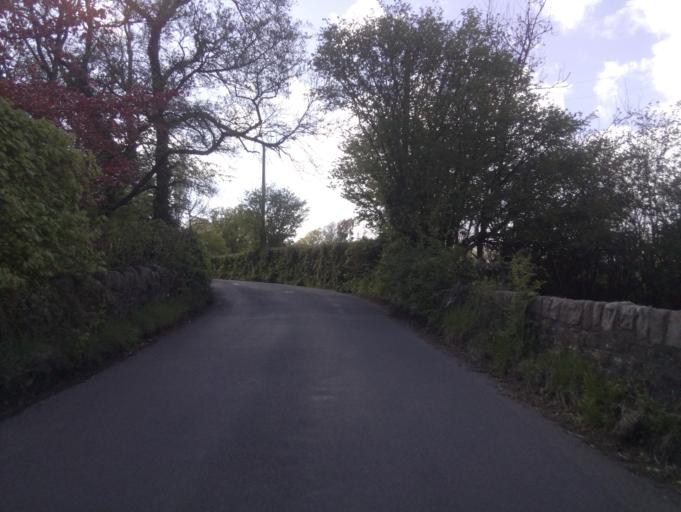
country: GB
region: Wales
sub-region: Caerphilly County Borough
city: Bedwas
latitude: 51.5714
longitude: -3.1721
